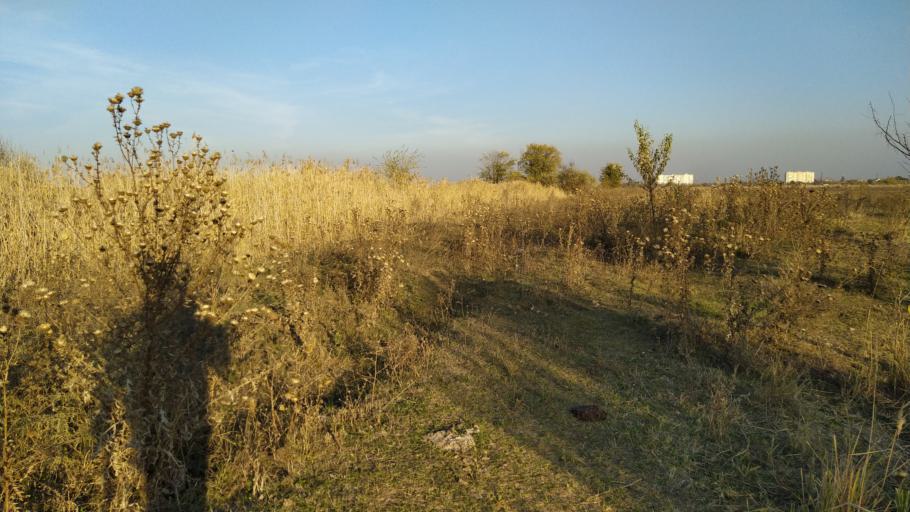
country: RU
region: Rostov
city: Bataysk
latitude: 47.1216
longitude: 39.7147
